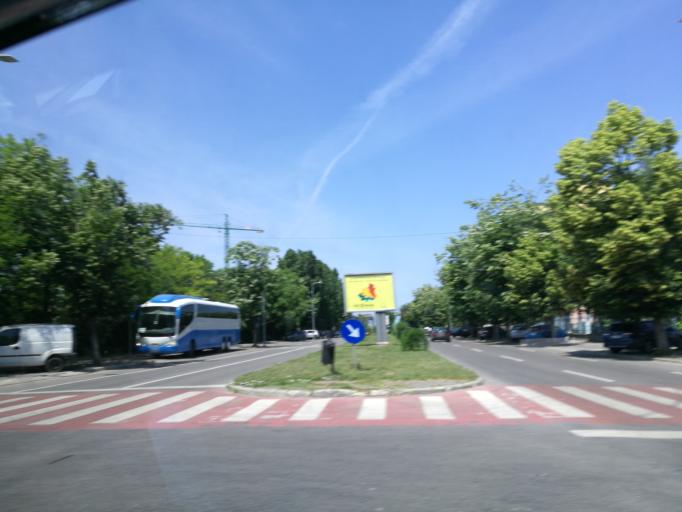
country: RO
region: Constanta
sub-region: Municipiul Constanta
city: Constanta
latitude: 44.2089
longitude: 28.6435
